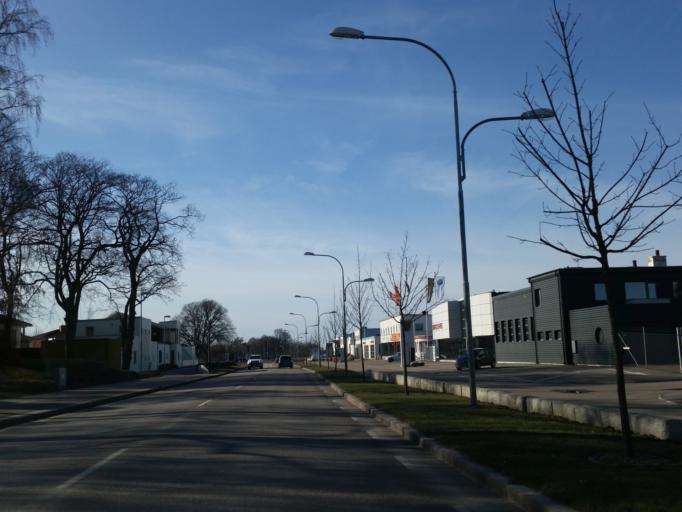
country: SE
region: Kalmar
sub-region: Kalmar Kommun
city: Kalmar
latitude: 56.6647
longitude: 16.3325
